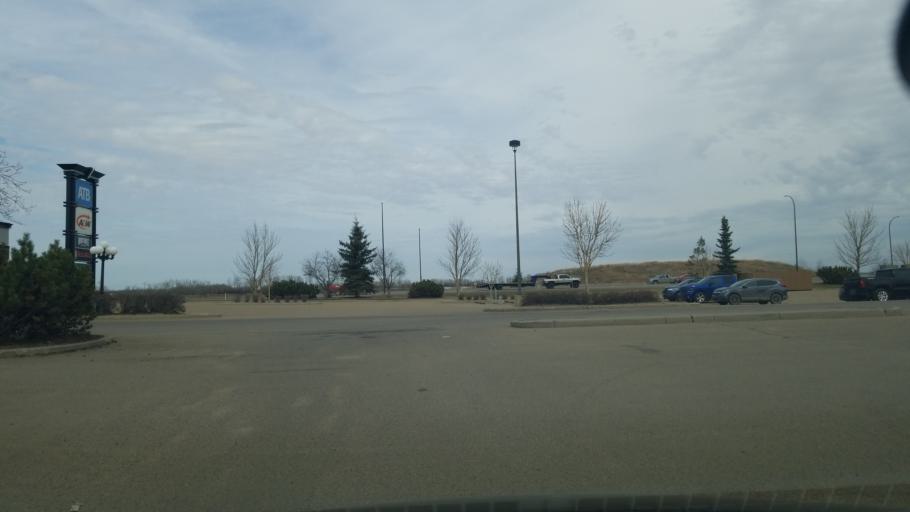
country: CA
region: Saskatchewan
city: Lloydminster
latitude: 53.2770
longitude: -110.0498
